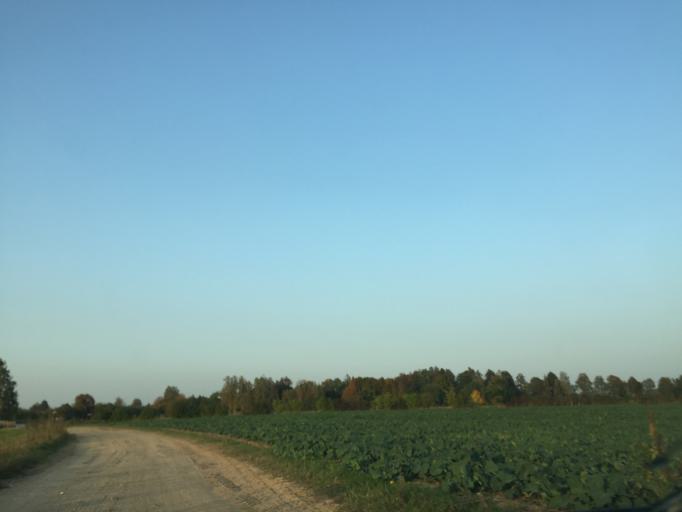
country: LV
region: Lielvarde
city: Lielvarde
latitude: 56.7912
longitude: 24.8182
